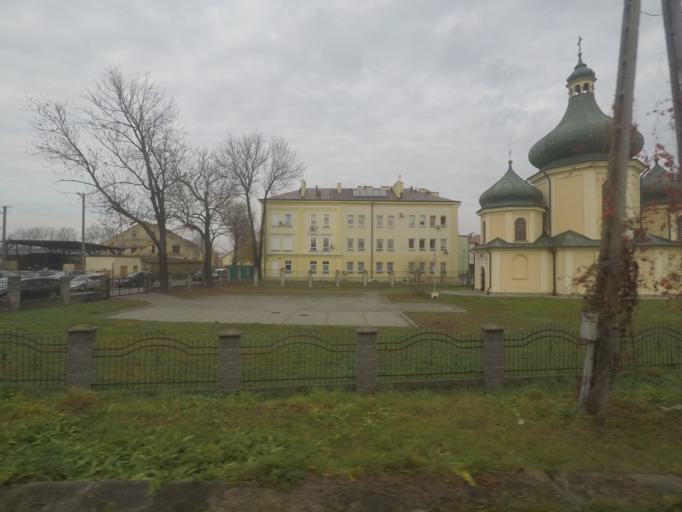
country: PL
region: Subcarpathian Voivodeship
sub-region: Przemysl
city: Przemysl
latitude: 49.7839
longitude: 22.7901
